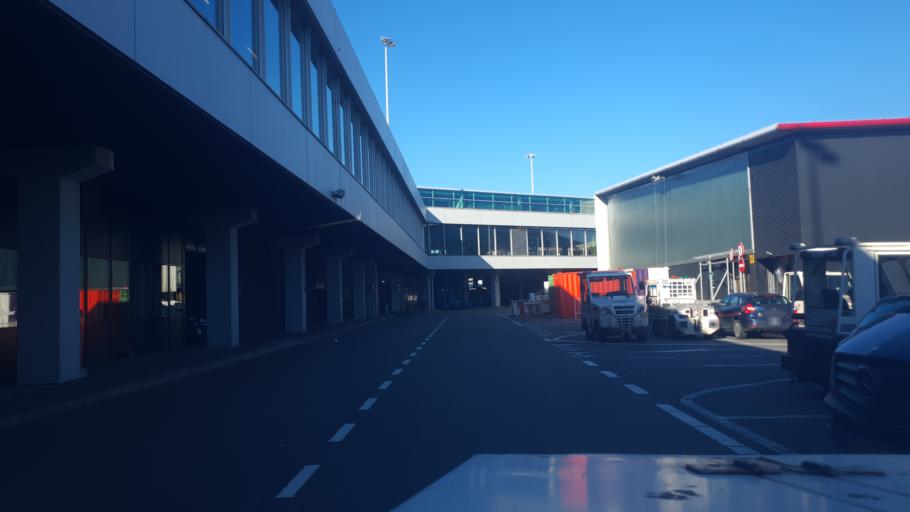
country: NL
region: North Holland
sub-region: Gemeente Aalsmeer
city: Aalsmeer
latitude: 52.3077
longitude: 4.7711
